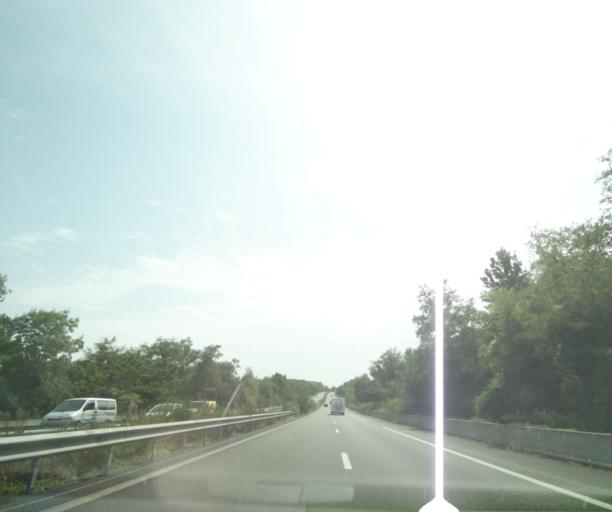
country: FR
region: Poitou-Charentes
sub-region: Departement de la Charente-Maritime
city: Saint-Savinien
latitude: 45.8693
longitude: -0.6225
